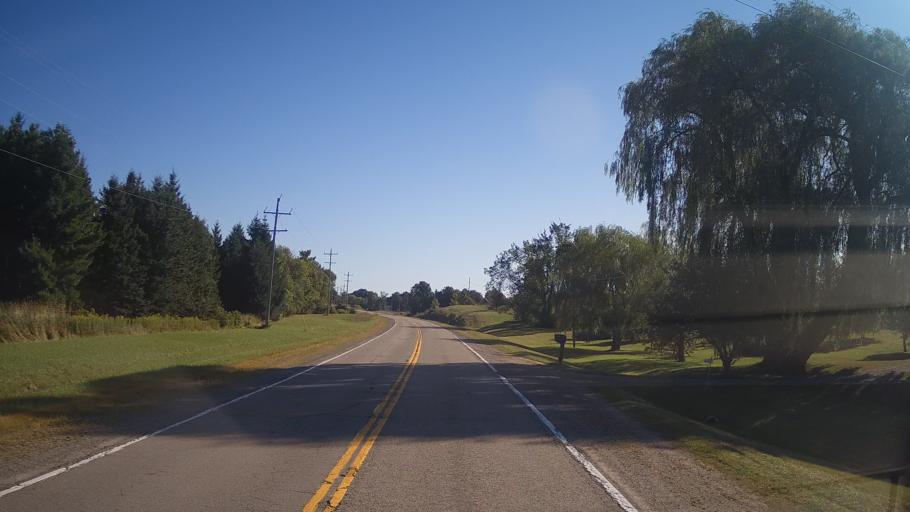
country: CA
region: Ontario
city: Gananoque
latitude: 44.6102
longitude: -76.0606
